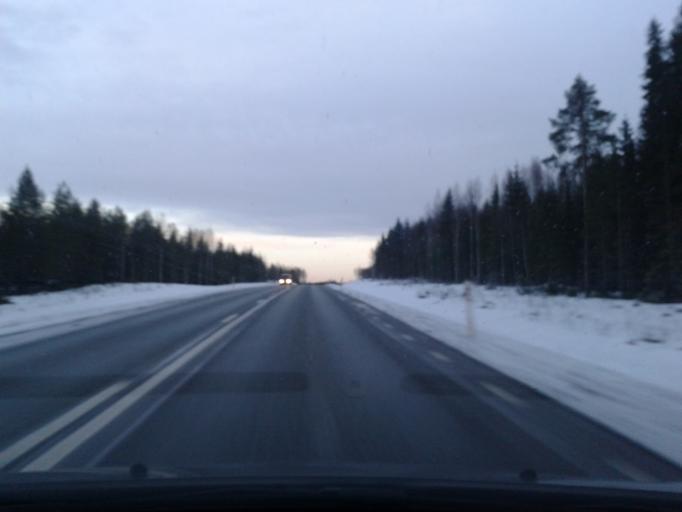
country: SE
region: Vaesternorrland
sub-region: Kramfors Kommun
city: Bollstabruk
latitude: 63.0607
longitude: 17.6013
